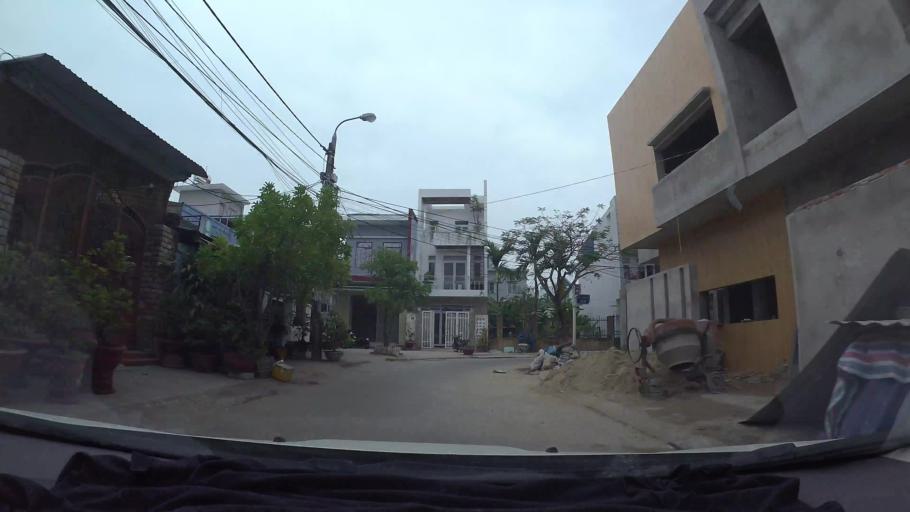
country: VN
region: Da Nang
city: Thanh Khe
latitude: 16.0541
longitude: 108.1783
